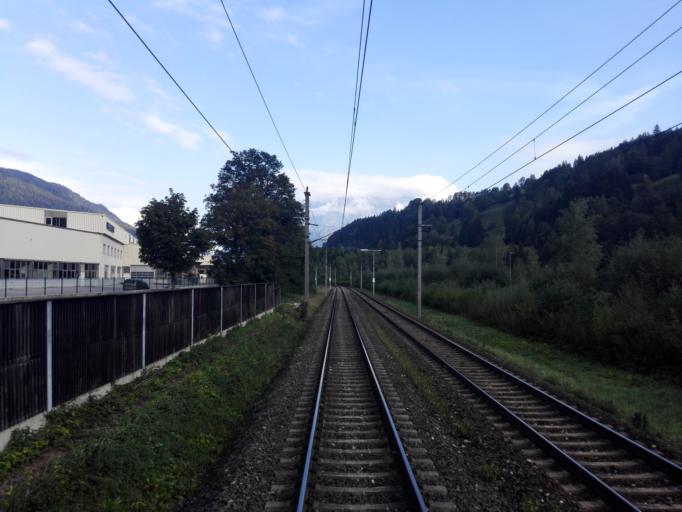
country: AT
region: Salzburg
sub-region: Politischer Bezirk Sankt Johann im Pongau
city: Bischofshofen
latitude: 47.3990
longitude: 13.2250
